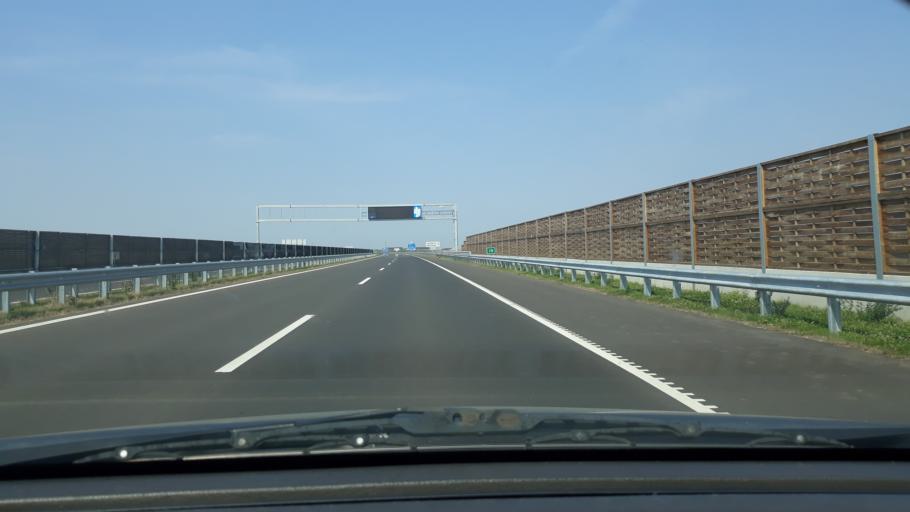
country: HU
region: Hajdu-Bihar
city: Berettyoujfalu
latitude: 47.2661
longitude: 21.5612
